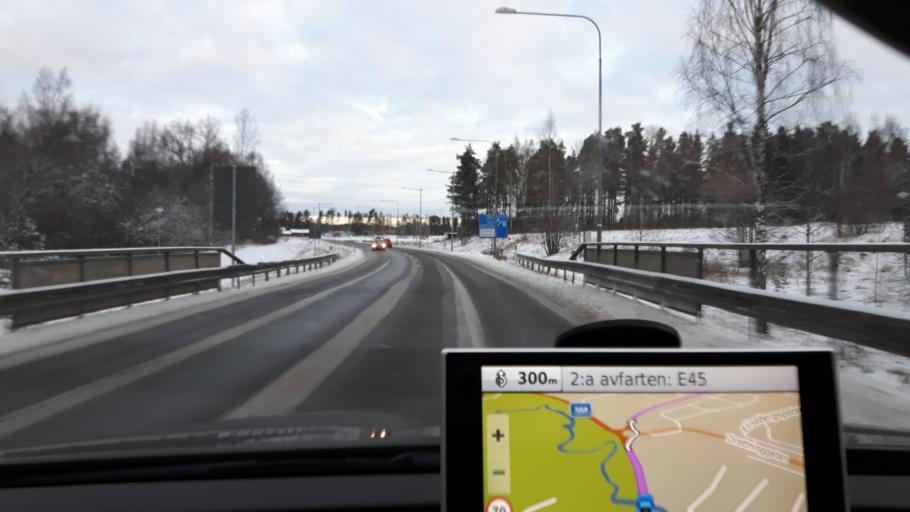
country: SE
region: Vaestra Goetaland
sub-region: Amals Kommun
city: Amal
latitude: 59.0523
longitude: 12.6773
